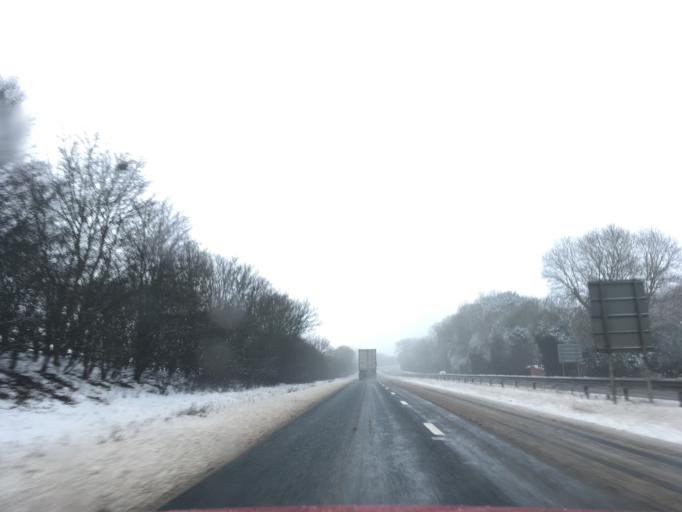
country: GB
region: England
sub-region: Warwickshire
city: Warwick
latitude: 52.2510
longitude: -1.6368
